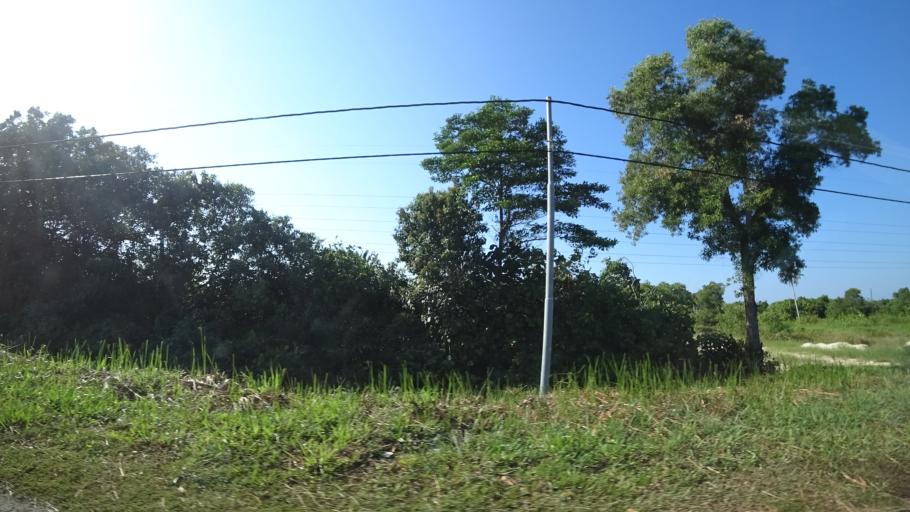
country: BN
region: Tutong
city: Tutong
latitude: 4.7013
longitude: 114.5231
